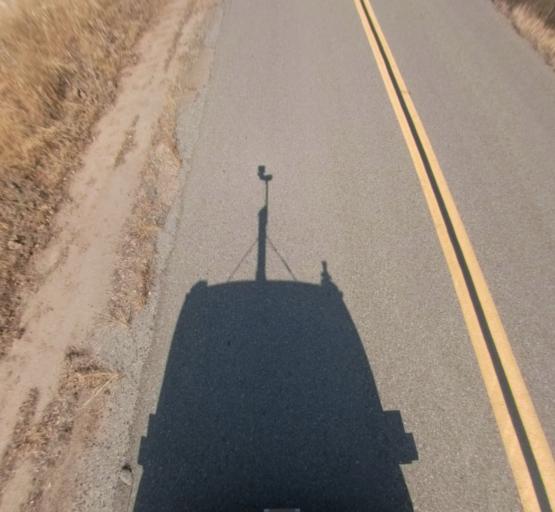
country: US
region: California
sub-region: Madera County
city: Yosemite Lakes
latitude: 37.1133
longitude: -119.6586
